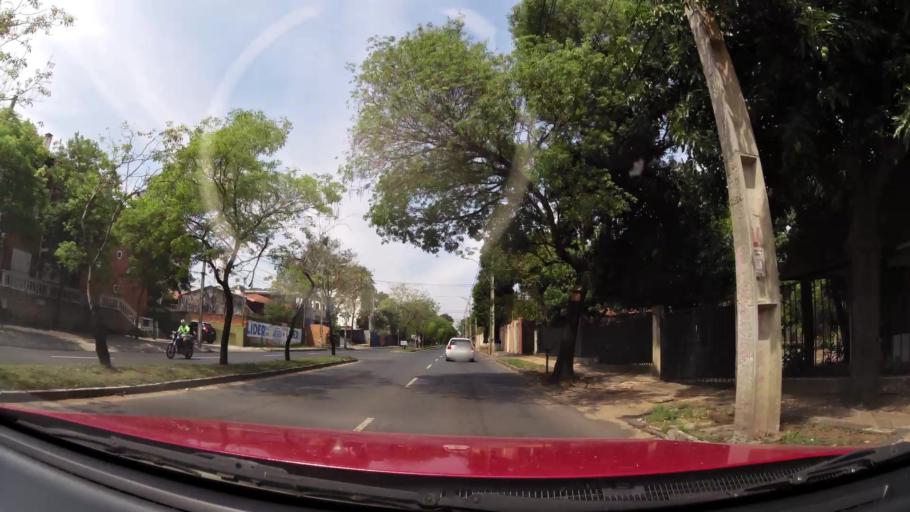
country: PY
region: Asuncion
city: Asuncion
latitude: -25.2770
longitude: -57.5859
